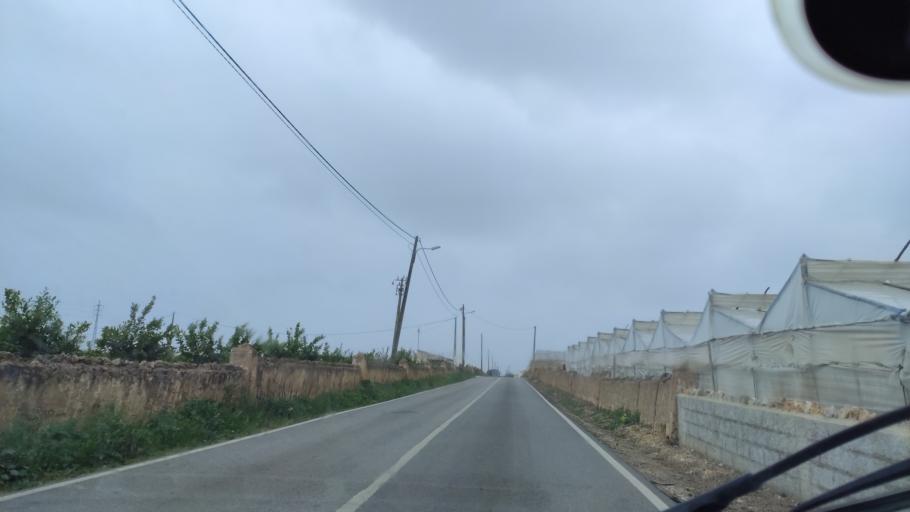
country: PT
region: Faro
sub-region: Faro
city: Santa Barbara de Nexe
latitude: 37.0731
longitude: -7.9412
